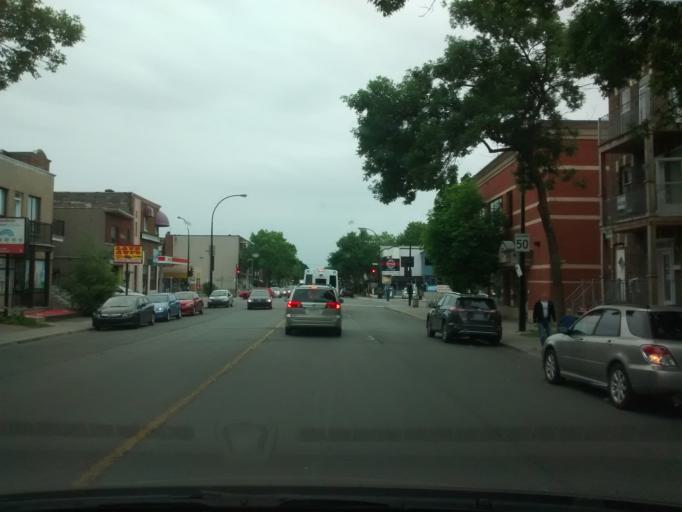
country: CA
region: Quebec
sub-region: Montreal
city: Montreal
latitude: 45.5472
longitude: -73.5858
